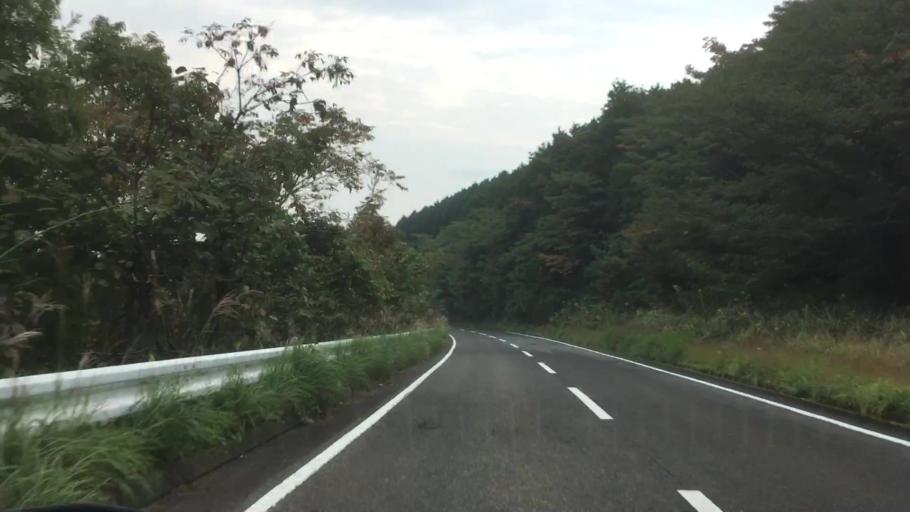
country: JP
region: Nagasaki
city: Sasebo
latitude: 33.0375
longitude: 129.6883
